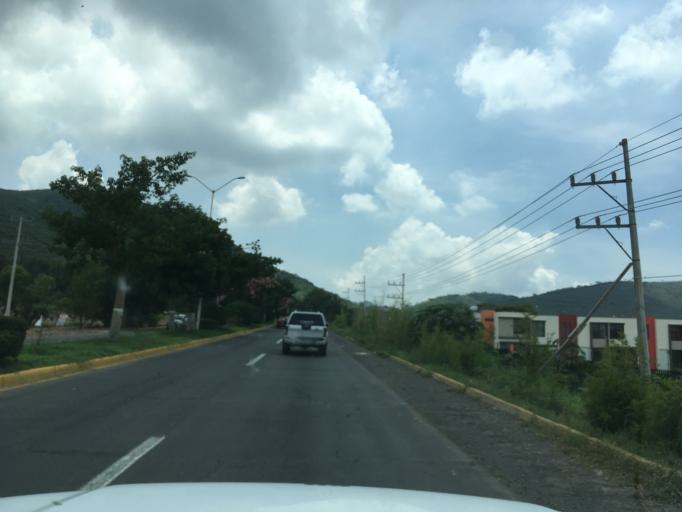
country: MX
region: Jalisco
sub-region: Tlajomulco de Zuniga
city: Santa Cruz de las Flores
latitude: 20.4905
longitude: -103.4767
